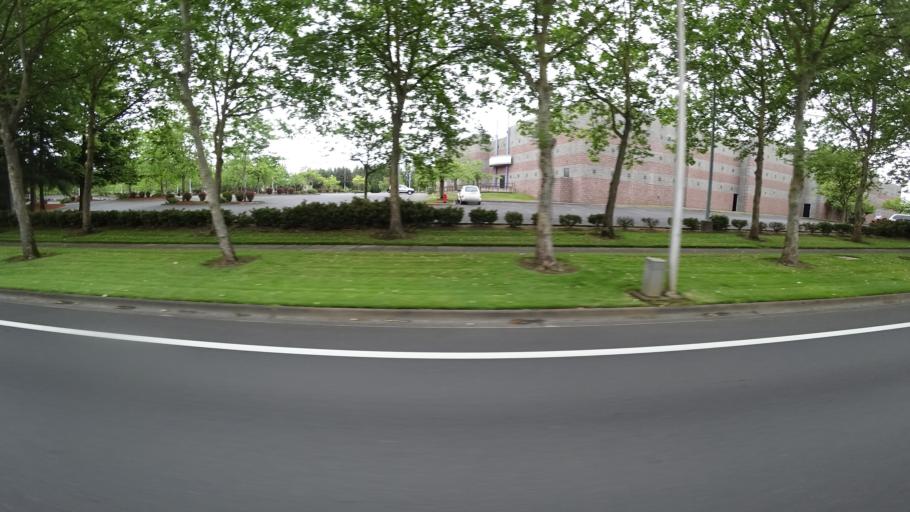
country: US
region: Oregon
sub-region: Washington County
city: Rockcreek
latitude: 45.5388
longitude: -122.8727
